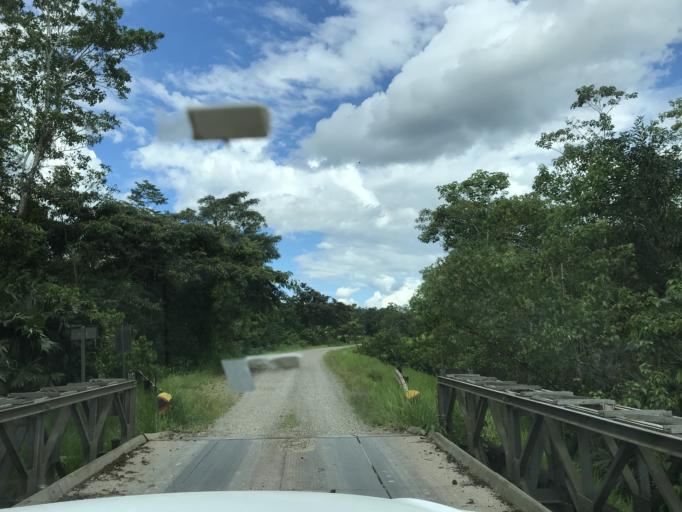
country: EC
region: Orellana
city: Puerto Francisco de Orellana
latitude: -0.6092
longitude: -76.4676
